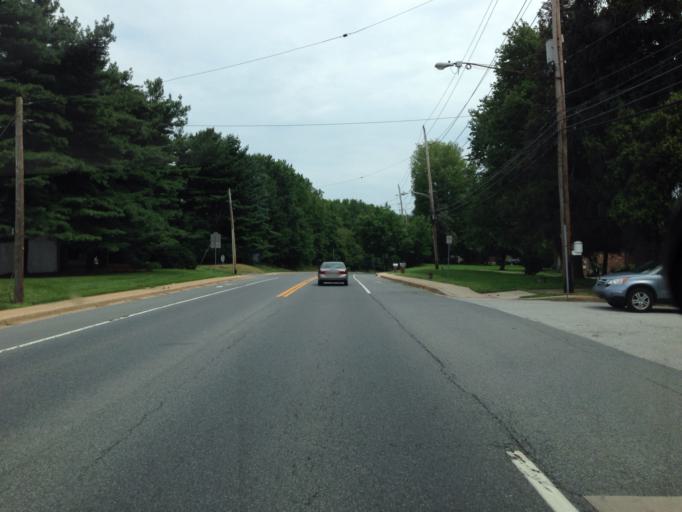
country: US
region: Delaware
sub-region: New Castle County
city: Newark
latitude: 39.6919
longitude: -75.7623
